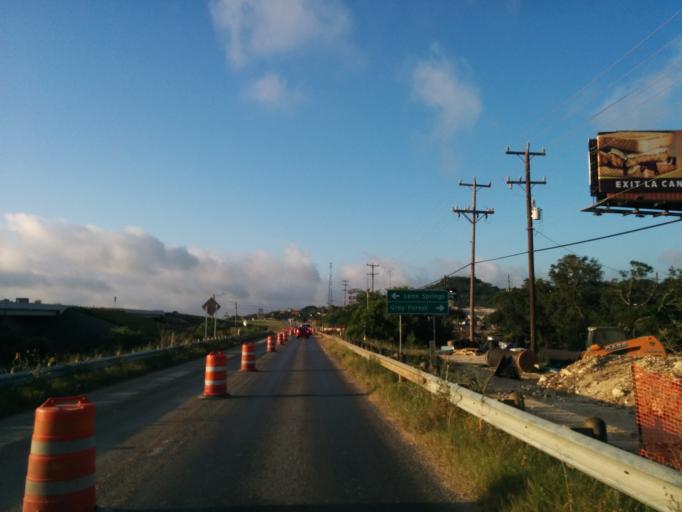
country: US
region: Texas
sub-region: Bexar County
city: Cross Mountain
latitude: 29.6679
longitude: -98.6329
